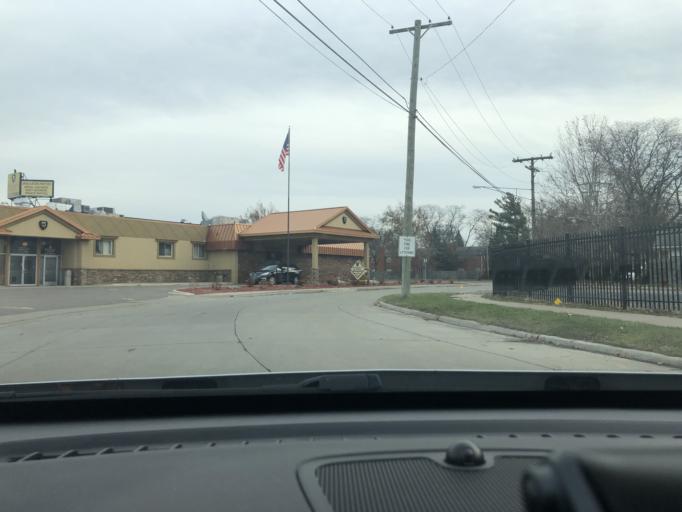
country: US
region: Michigan
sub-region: Wayne County
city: Dearborn Heights
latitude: 42.3419
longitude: -83.2400
